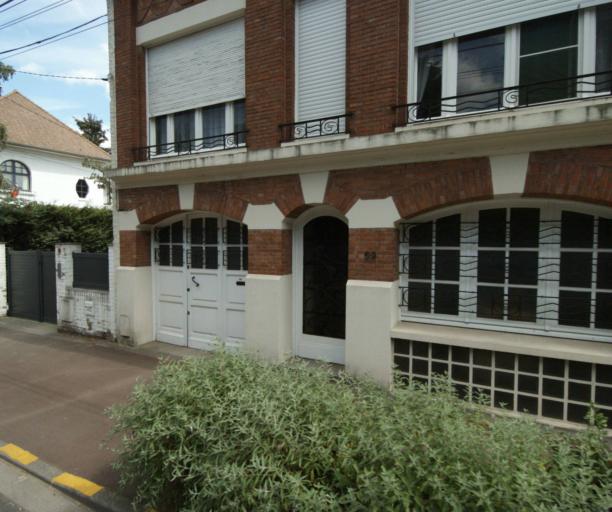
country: FR
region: Nord-Pas-de-Calais
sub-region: Departement du Nord
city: Mouvaux
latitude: 50.6931
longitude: 3.1349
